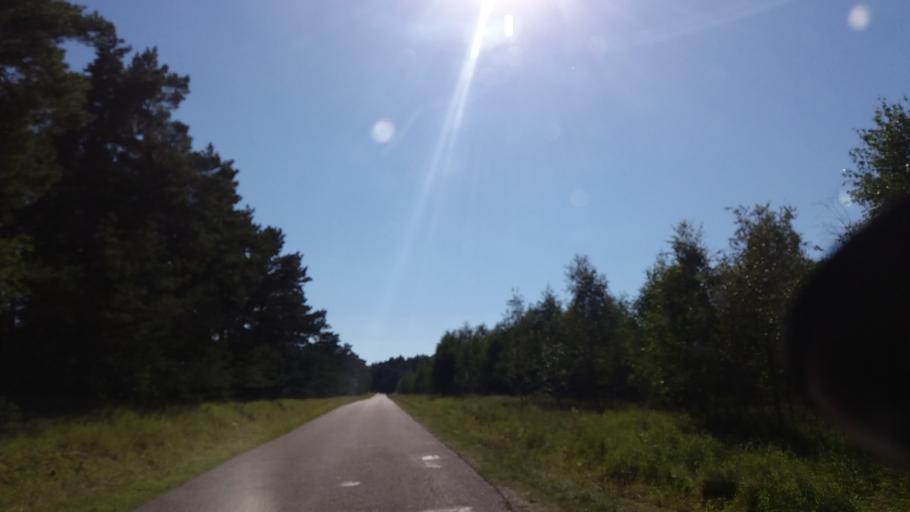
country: PL
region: West Pomeranian Voivodeship
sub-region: Powiat szczecinecki
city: Borne Sulinowo
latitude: 53.5720
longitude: 16.5276
